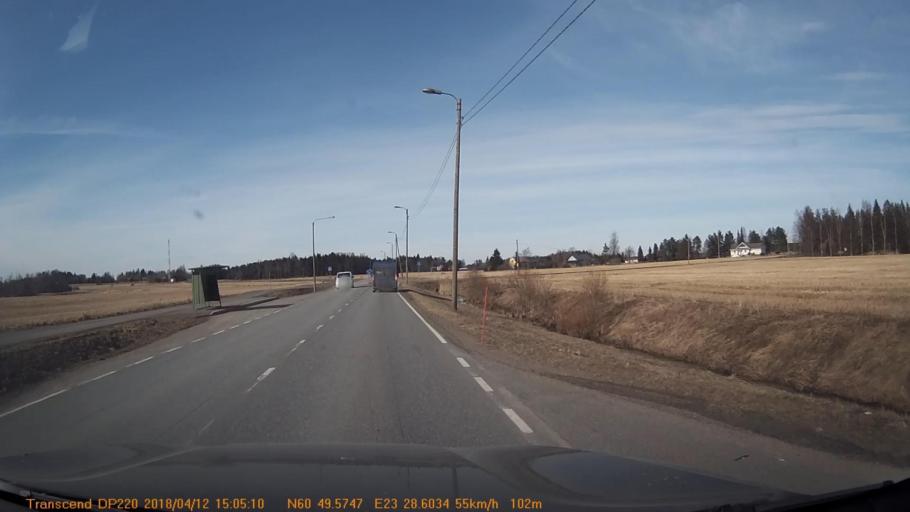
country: FI
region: Haeme
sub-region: Forssa
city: Jokioinen
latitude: 60.8264
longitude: 23.4767
